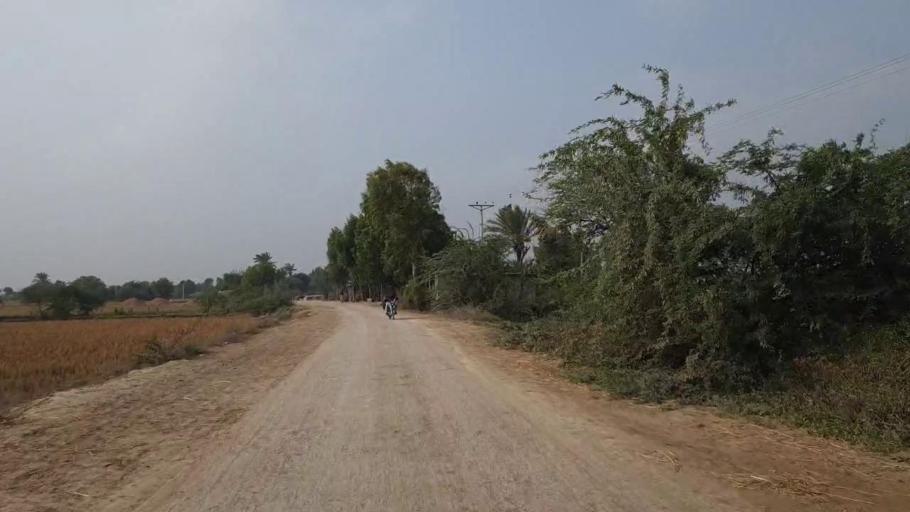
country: PK
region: Sindh
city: Matli
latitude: 24.9785
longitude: 68.6177
